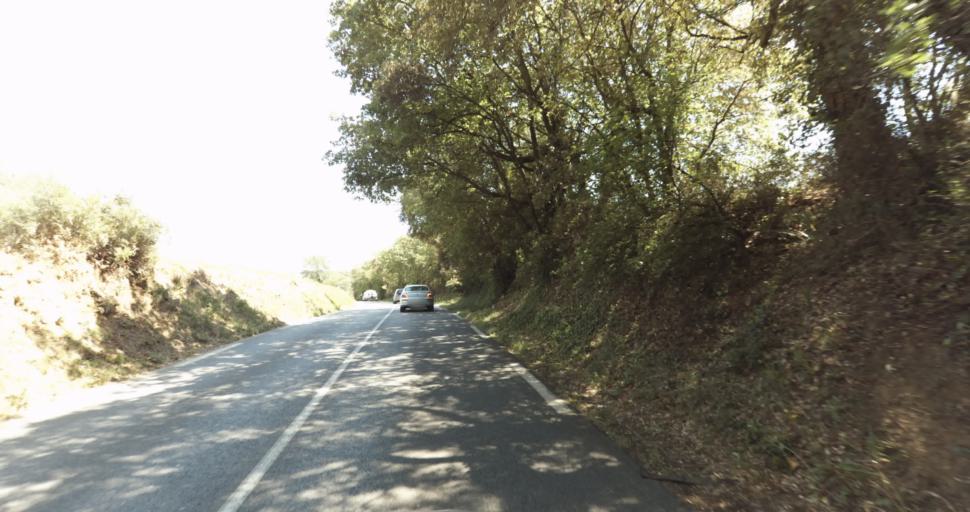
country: FR
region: Provence-Alpes-Cote d'Azur
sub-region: Departement du Var
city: Hyeres
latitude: 43.1523
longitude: 6.1301
